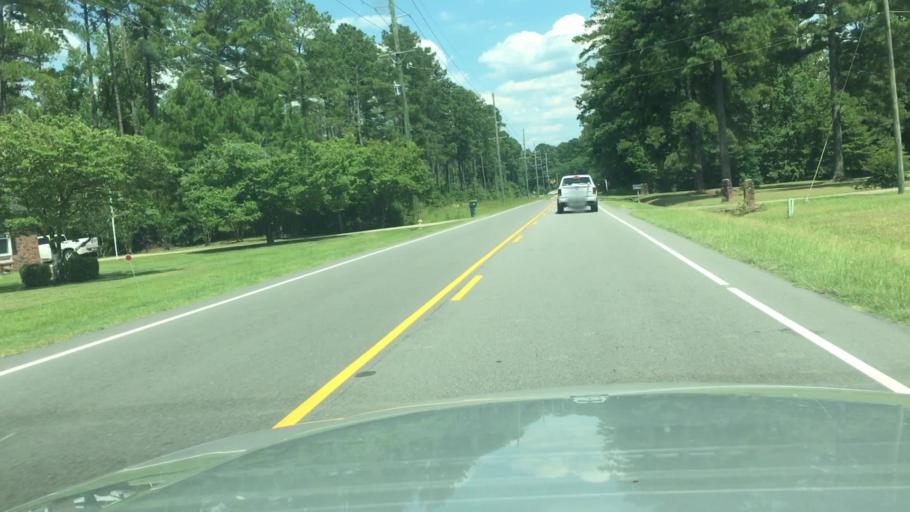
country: US
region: North Carolina
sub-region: Cumberland County
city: Hope Mills
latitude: 34.9498
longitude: -78.8493
